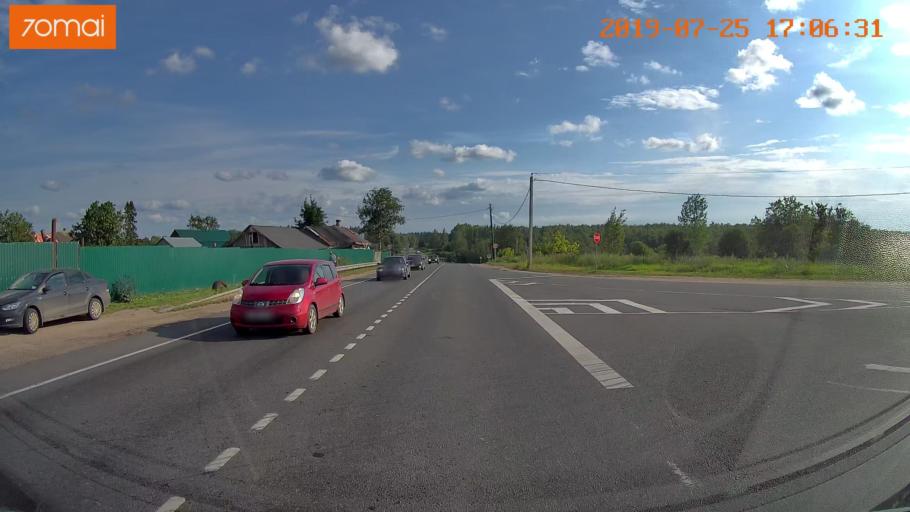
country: RU
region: Ivanovo
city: Furmanov
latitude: 57.1644
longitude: 41.0700
